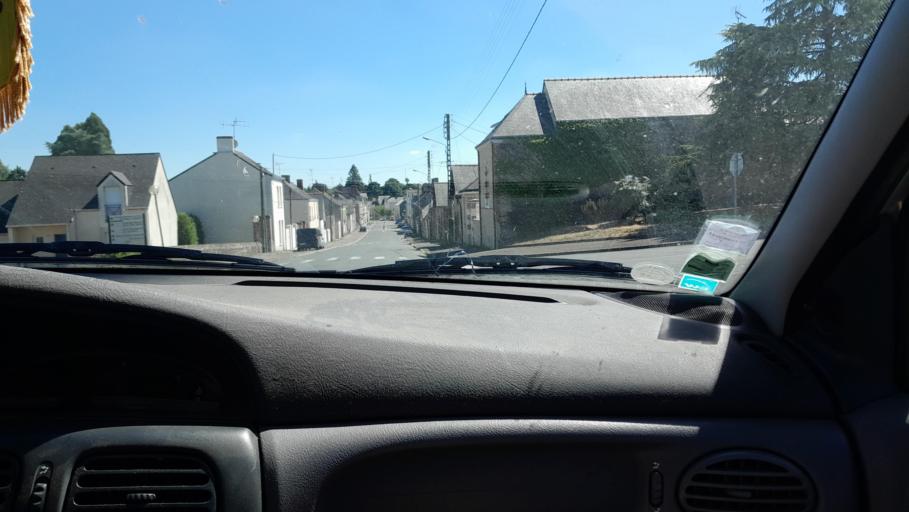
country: FR
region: Pays de la Loire
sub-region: Departement de la Loire-Atlantique
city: Saint-Mars-la-Jaille
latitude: 47.5272
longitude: -1.1851
